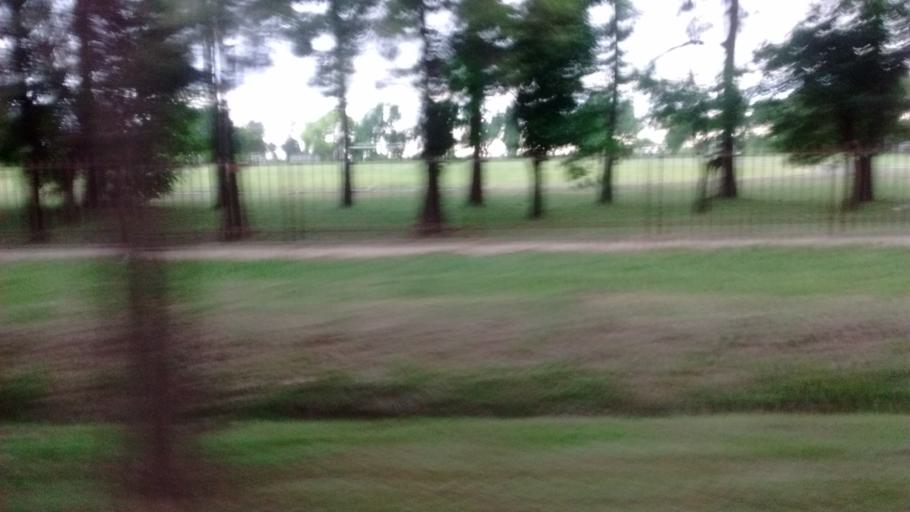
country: AR
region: Santa Fe
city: Funes
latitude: -32.9295
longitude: -60.8181
